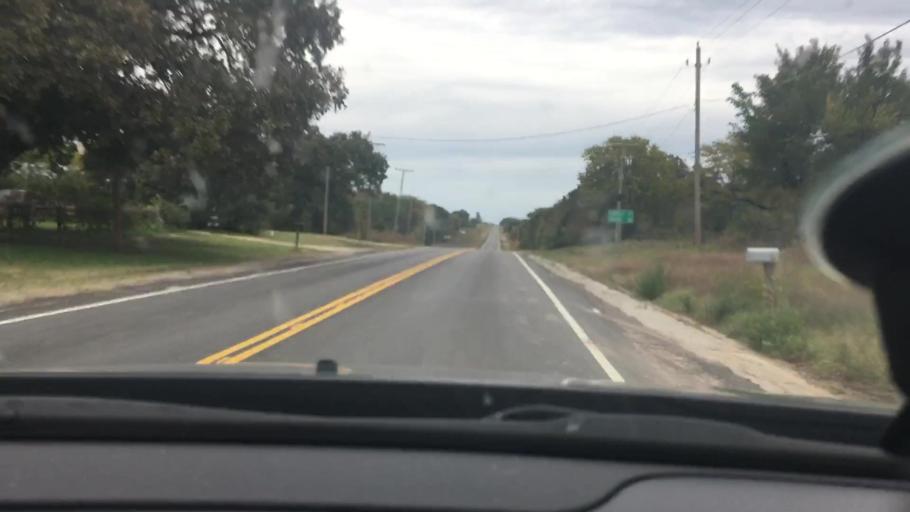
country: US
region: Oklahoma
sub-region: Coal County
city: Coalgate
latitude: 34.3780
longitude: -96.4245
